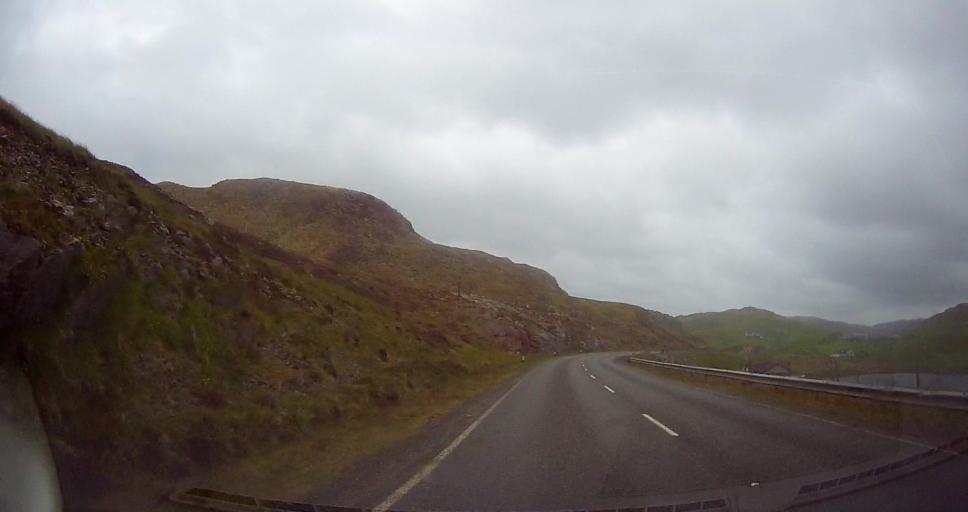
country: GB
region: Scotland
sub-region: Shetland Islands
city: Lerwick
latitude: 60.4123
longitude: -1.3907
